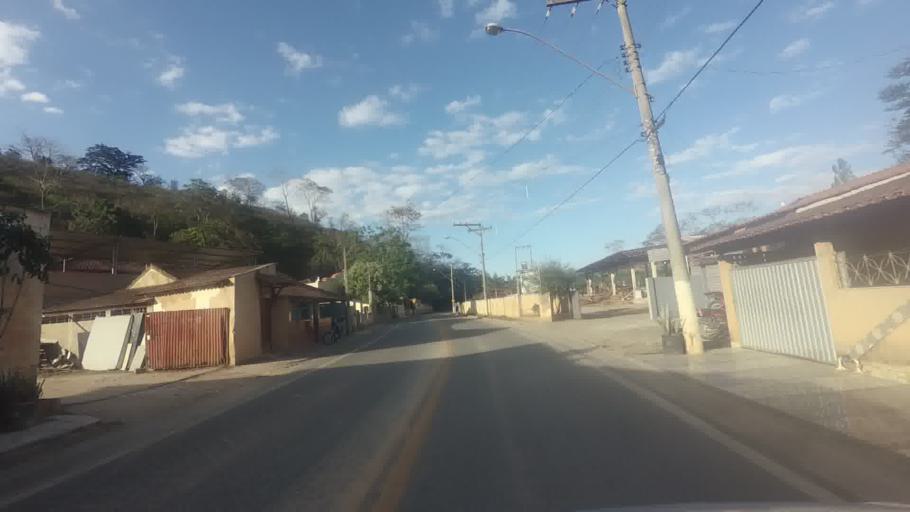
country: BR
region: Espirito Santo
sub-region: Mimoso Do Sul
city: Mimoso do Sul
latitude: -20.9450
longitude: -41.3362
